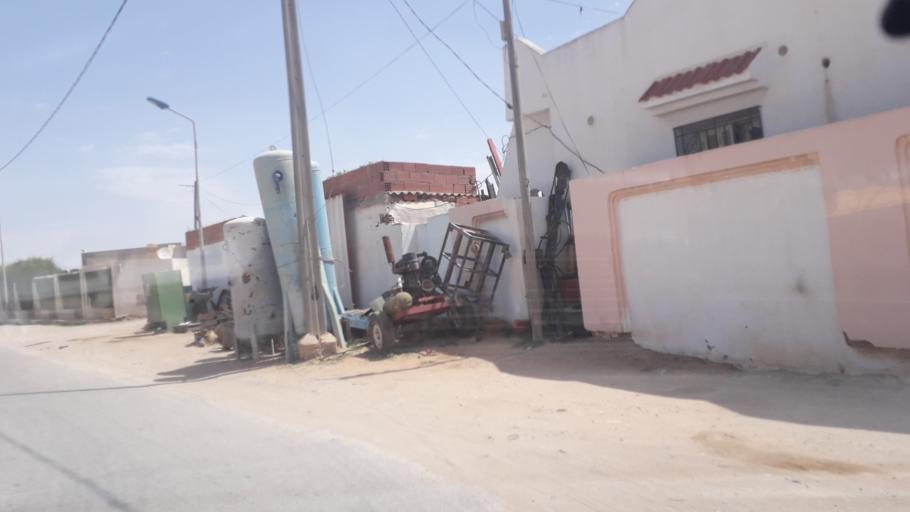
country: TN
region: Safaqis
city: Al Qarmadah
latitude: 34.8260
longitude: 10.7644
